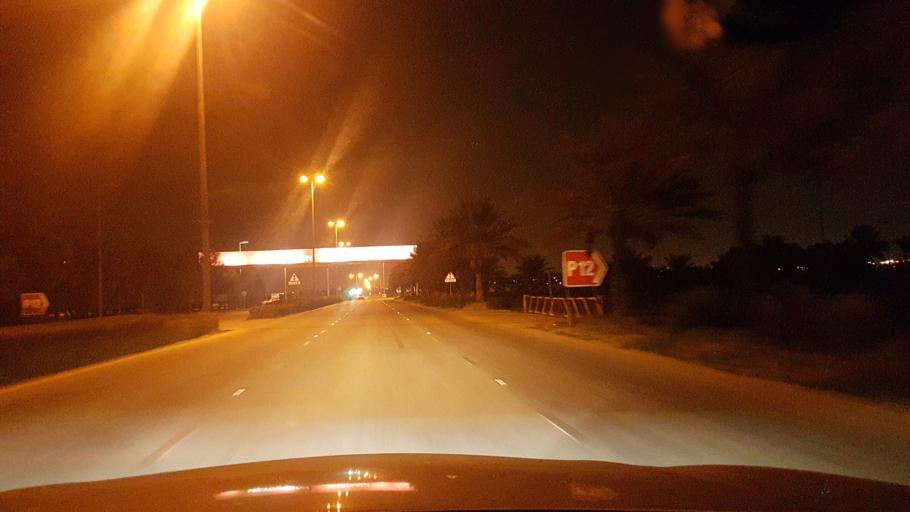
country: BH
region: Central Governorate
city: Dar Kulayb
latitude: 26.0362
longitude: 50.5053
